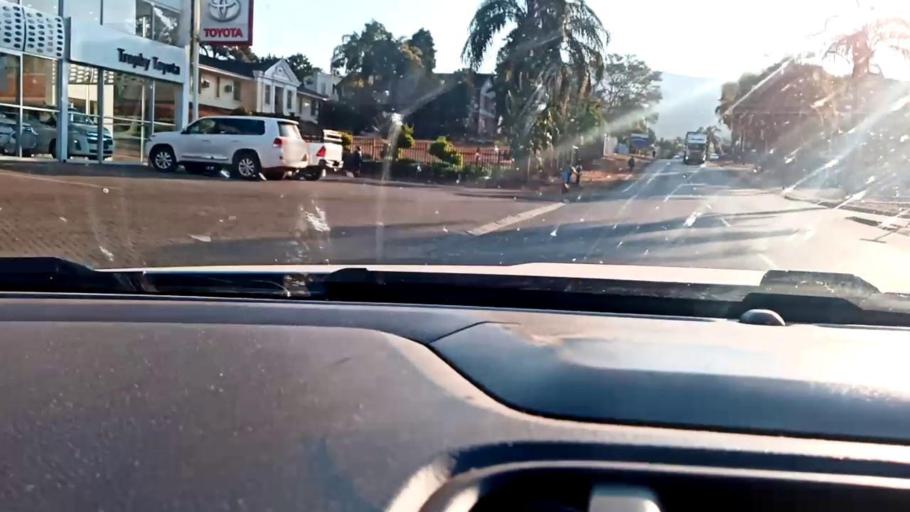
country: ZA
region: Limpopo
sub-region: Mopani District Municipality
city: Duiwelskloof
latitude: -23.6950
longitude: 30.1463
